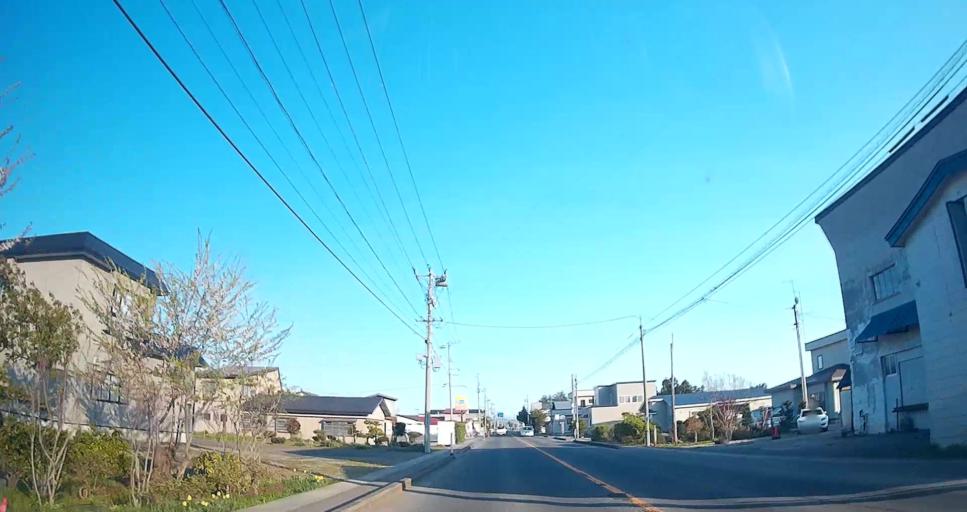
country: JP
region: Aomori
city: Mutsu
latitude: 41.2742
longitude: 141.2152
